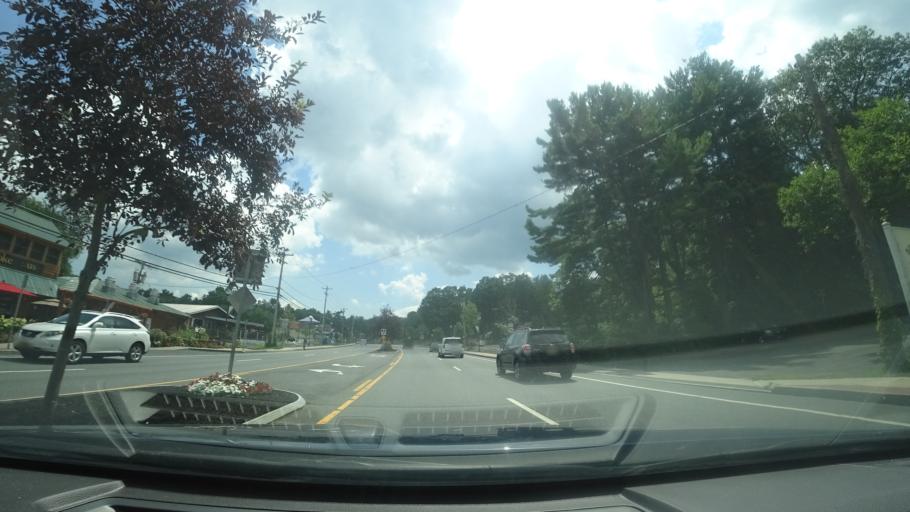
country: US
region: New York
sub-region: Warren County
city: Glens Falls North
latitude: 43.4080
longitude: -73.7107
